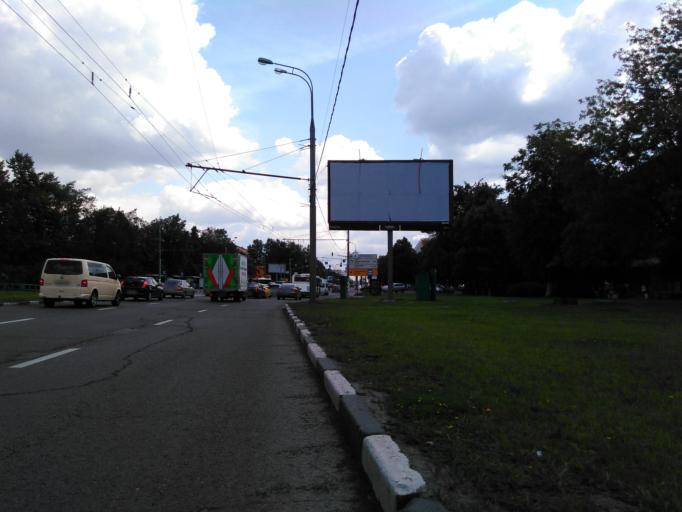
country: RU
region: Moskovskaya
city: Cheremushki
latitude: 55.6756
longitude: 37.5690
